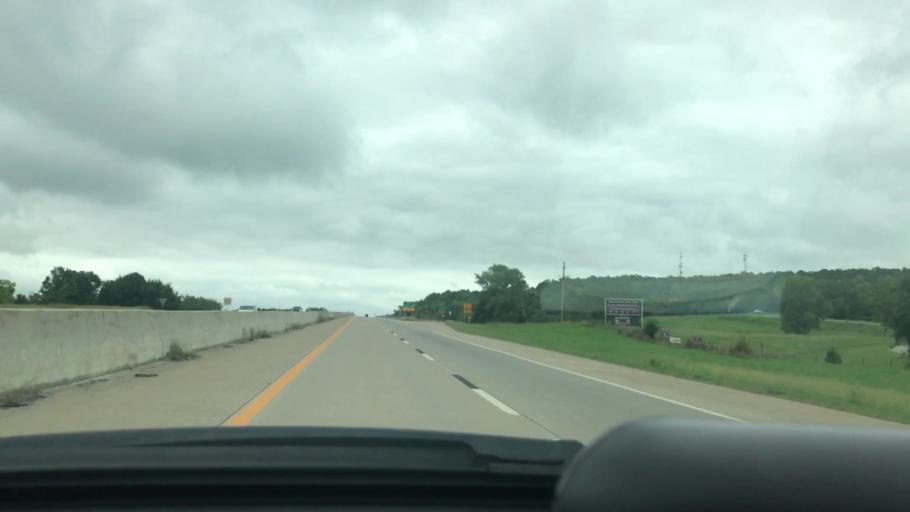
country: US
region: Oklahoma
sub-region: McIntosh County
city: Eufaula
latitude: 35.1682
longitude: -95.6513
